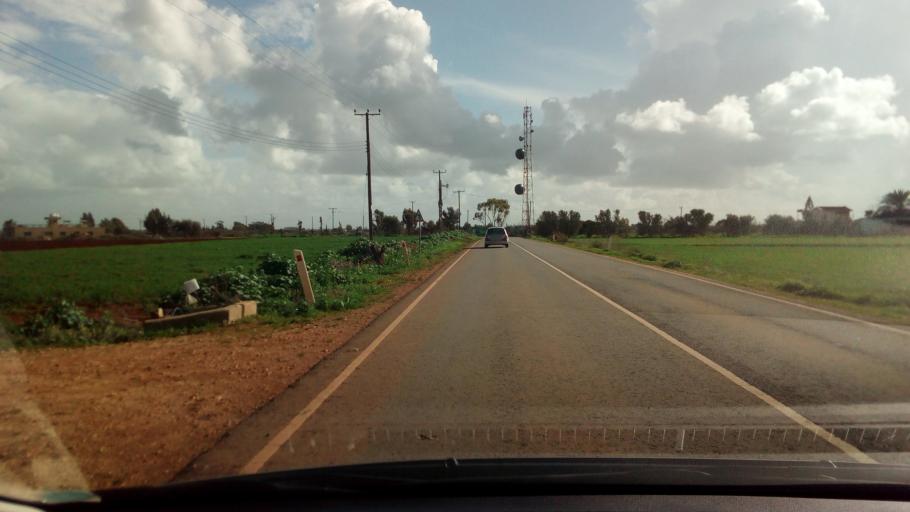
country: CY
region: Ammochostos
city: Achna
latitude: 35.0569
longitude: 33.8072
